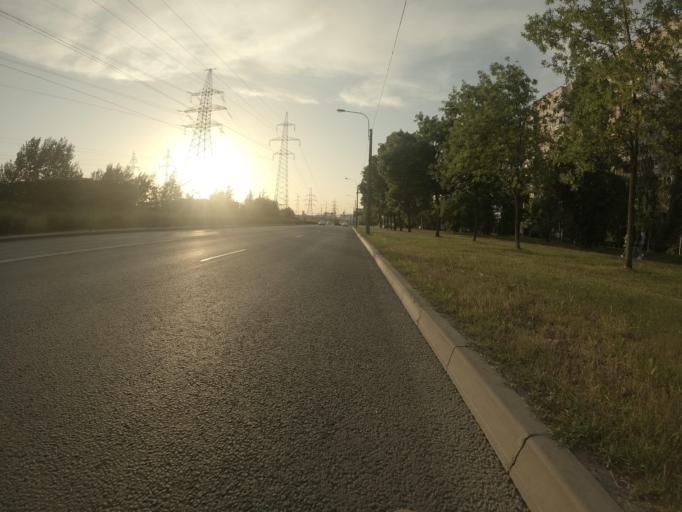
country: RU
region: St.-Petersburg
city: Krasnogvargeisky
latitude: 59.9400
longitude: 30.4674
